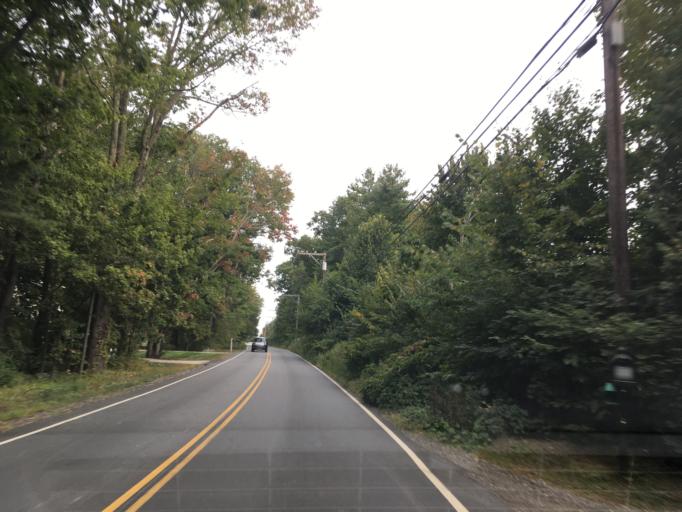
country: US
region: New Hampshire
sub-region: Rockingham County
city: Stratham Station
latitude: 43.0182
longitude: -70.8935
